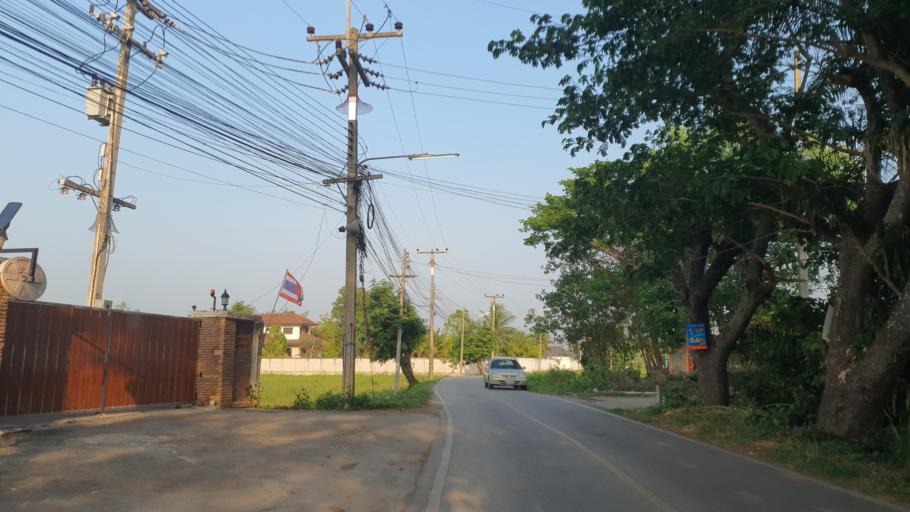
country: TH
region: Chiang Mai
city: San Pa Tong
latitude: 18.6339
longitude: 98.8924
